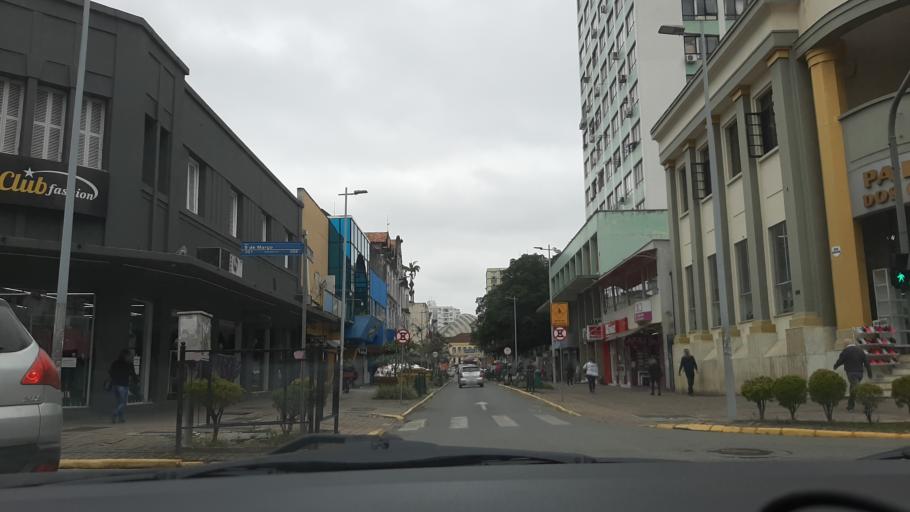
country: BR
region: Santa Catarina
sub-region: Joinville
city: Joinville
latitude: -26.3015
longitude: -48.8455
